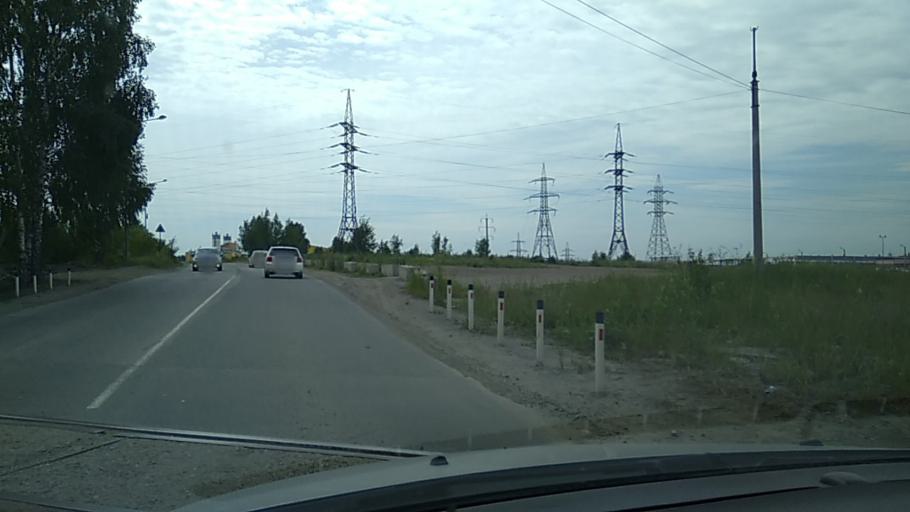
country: RU
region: Sverdlovsk
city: Verkhnyaya Pyshma
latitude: 56.9561
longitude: 60.5883
